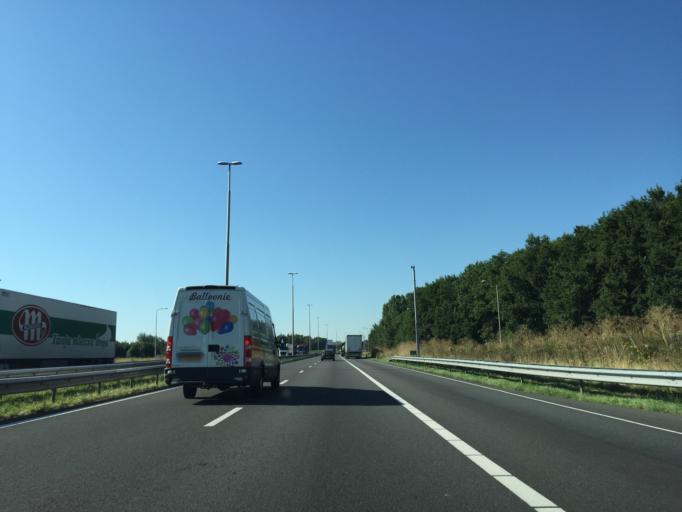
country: NL
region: Limburg
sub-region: Gemeente Sittard-Geleen
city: Born
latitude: 51.0383
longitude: 5.8248
